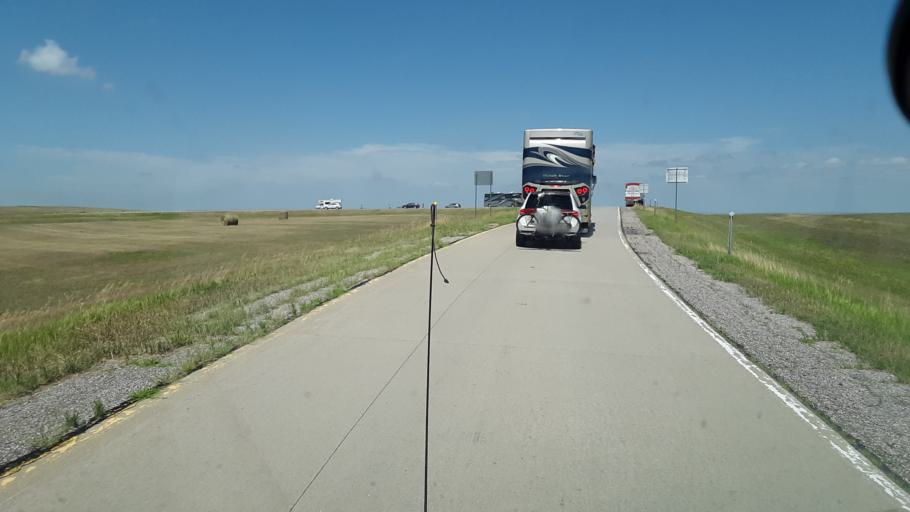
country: US
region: South Dakota
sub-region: Haakon County
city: Philip
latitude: 43.8373
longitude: -101.7746
